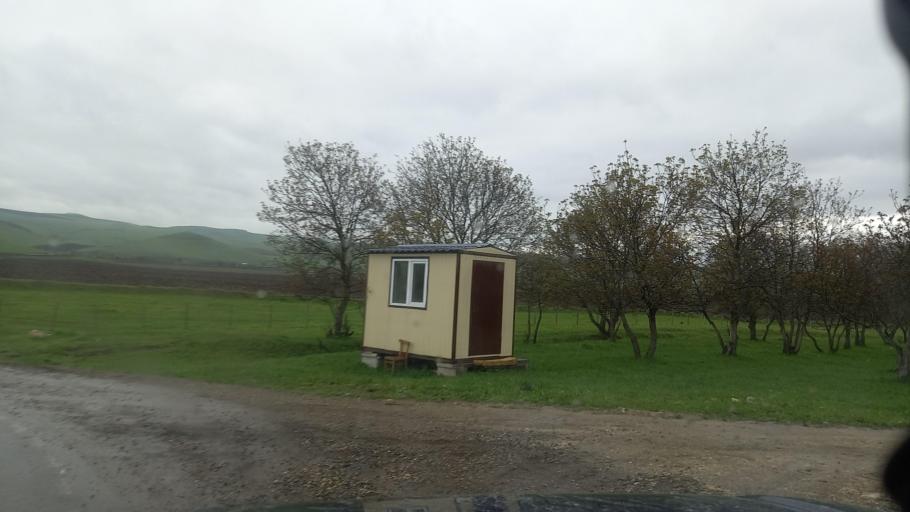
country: RU
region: Kabardino-Balkariya
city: Kamennomostskoye
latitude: 43.7061
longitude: 43.0705
